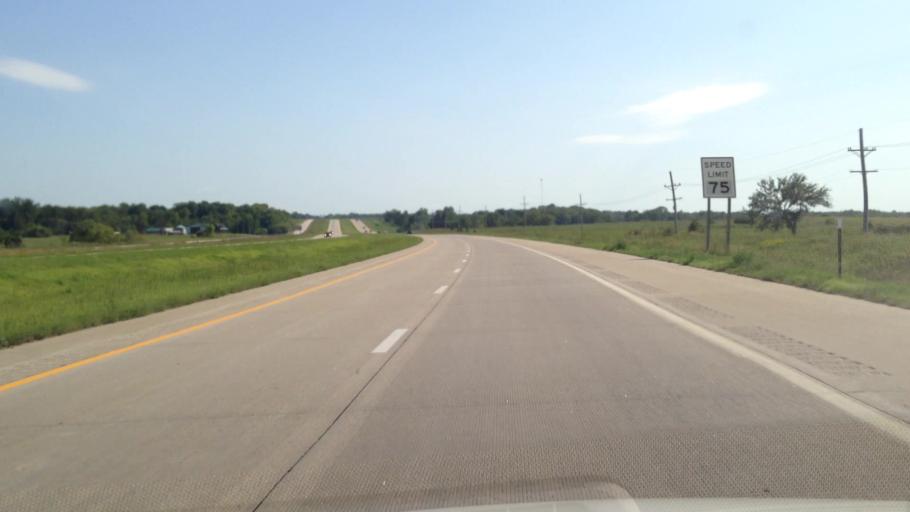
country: US
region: Kansas
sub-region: Linn County
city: Pleasanton
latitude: 38.2098
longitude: -94.7053
